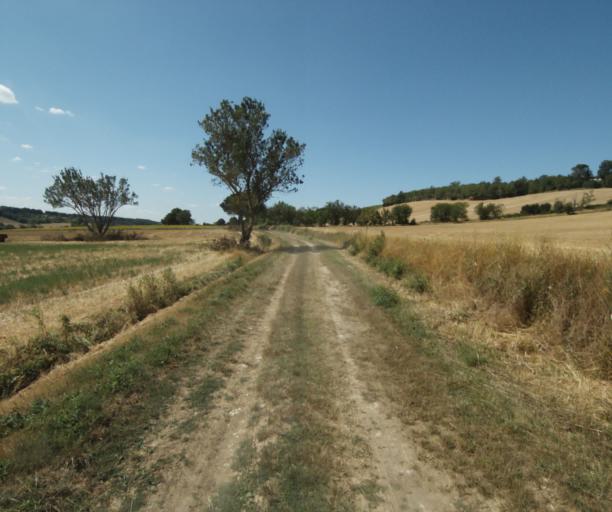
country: FR
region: Midi-Pyrenees
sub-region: Departement de la Haute-Garonne
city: Saint-Felix-Lauragais
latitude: 43.4961
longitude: 1.8753
